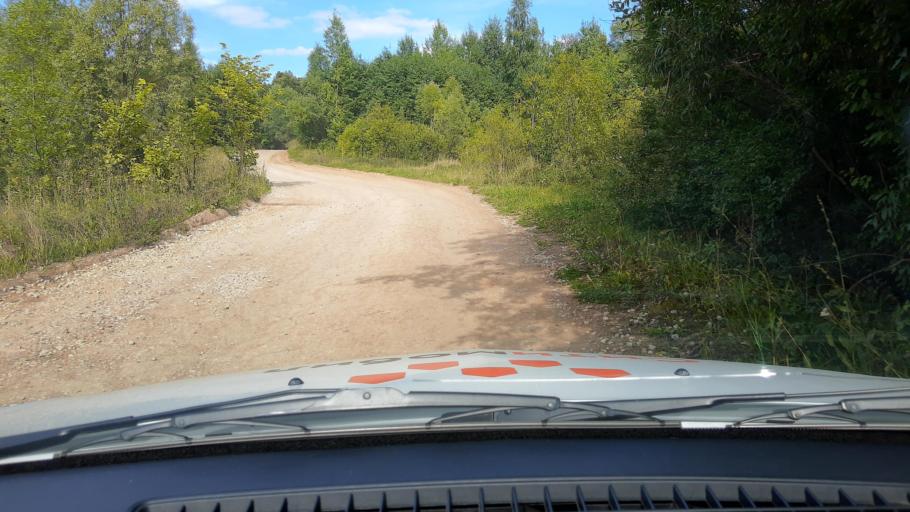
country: RU
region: Bashkortostan
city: Kabakovo
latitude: 54.7026
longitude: 56.1370
